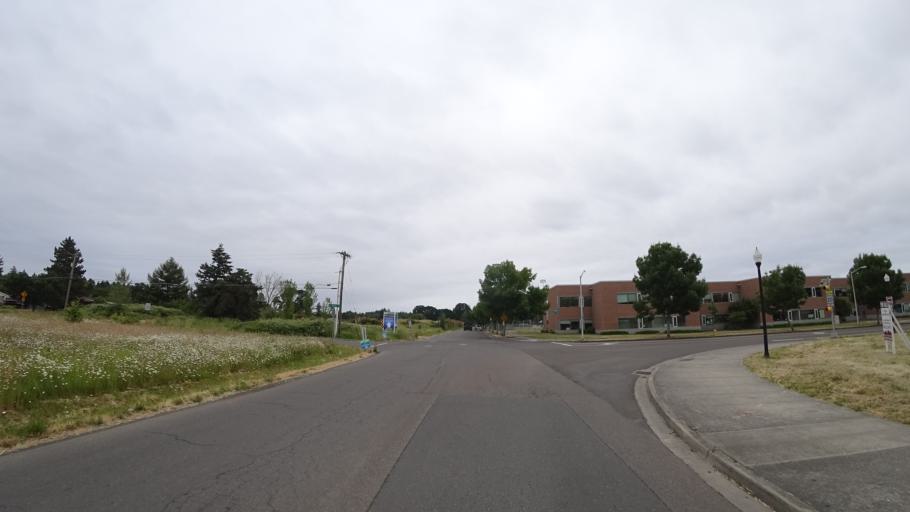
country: US
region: Oregon
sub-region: Washington County
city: Aloha
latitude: 45.4944
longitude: -122.9307
